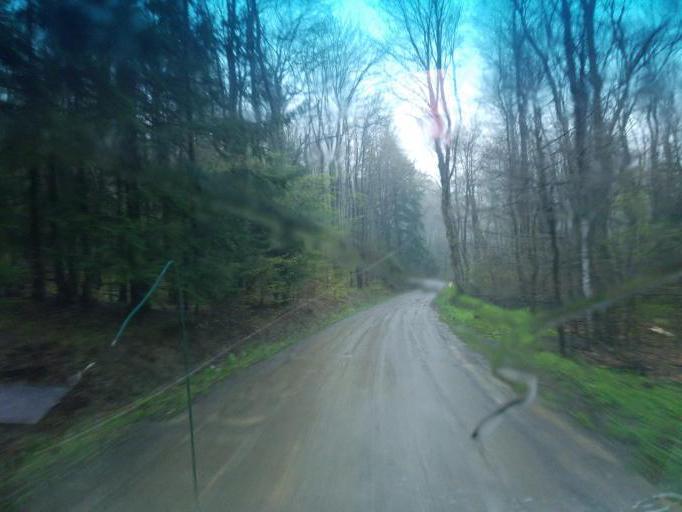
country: US
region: Pennsylvania
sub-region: Tioga County
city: Westfield
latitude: 41.9275
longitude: -77.7224
